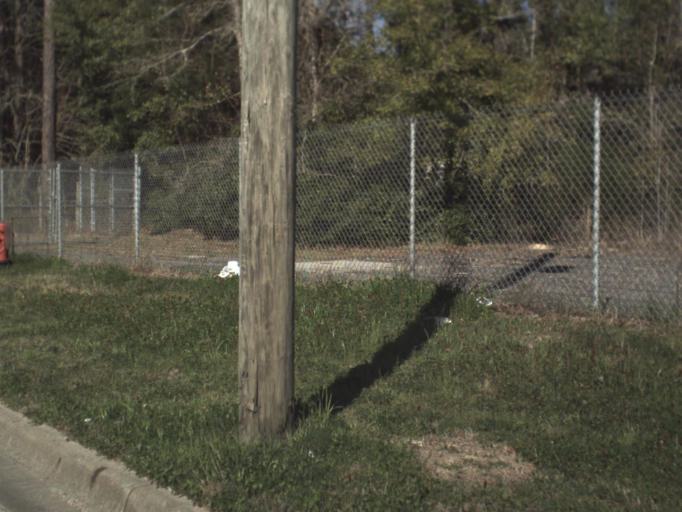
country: US
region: Florida
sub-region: Jackson County
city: Marianna
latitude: 30.7408
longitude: -85.1857
